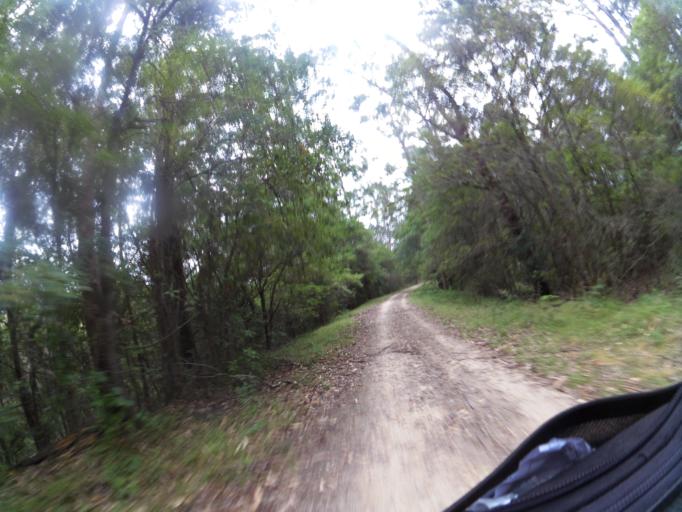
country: AU
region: Victoria
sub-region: East Gippsland
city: Lakes Entrance
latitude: -37.7294
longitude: 148.4253
